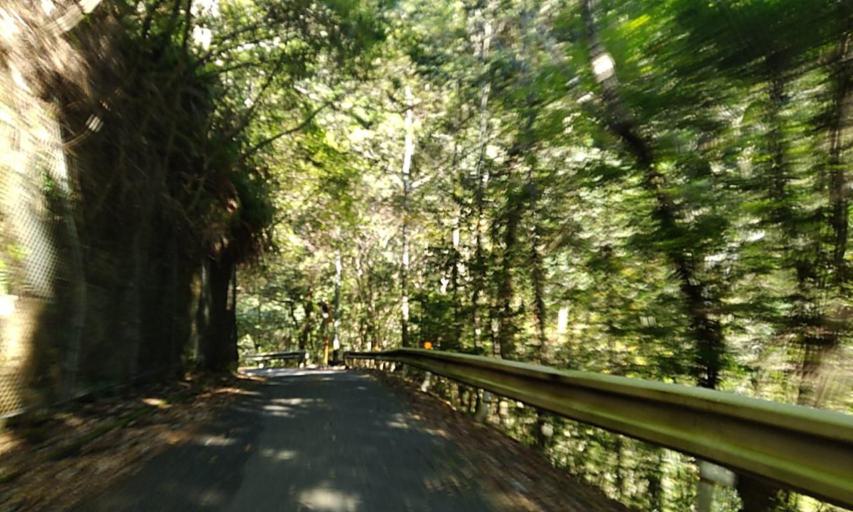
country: JP
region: Wakayama
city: Shingu
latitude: 33.9087
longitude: 135.9951
